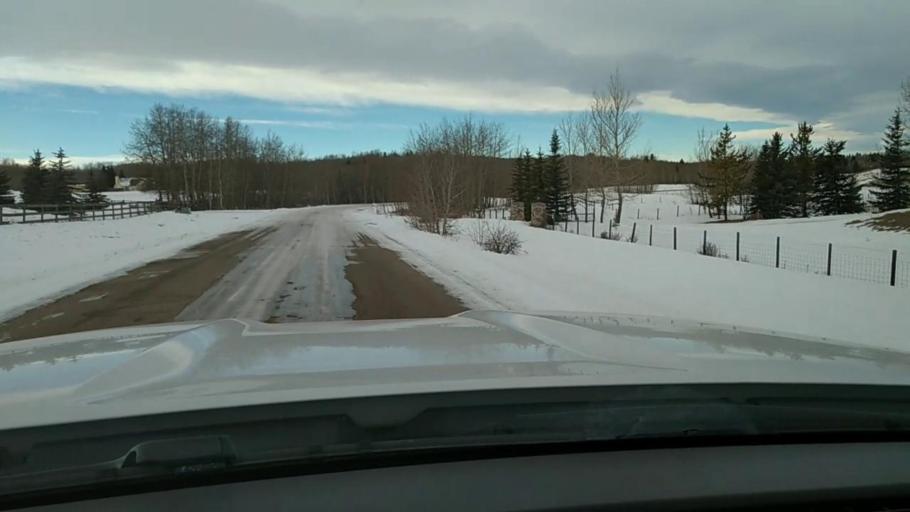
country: CA
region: Alberta
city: Cochrane
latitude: 51.1988
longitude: -114.2837
